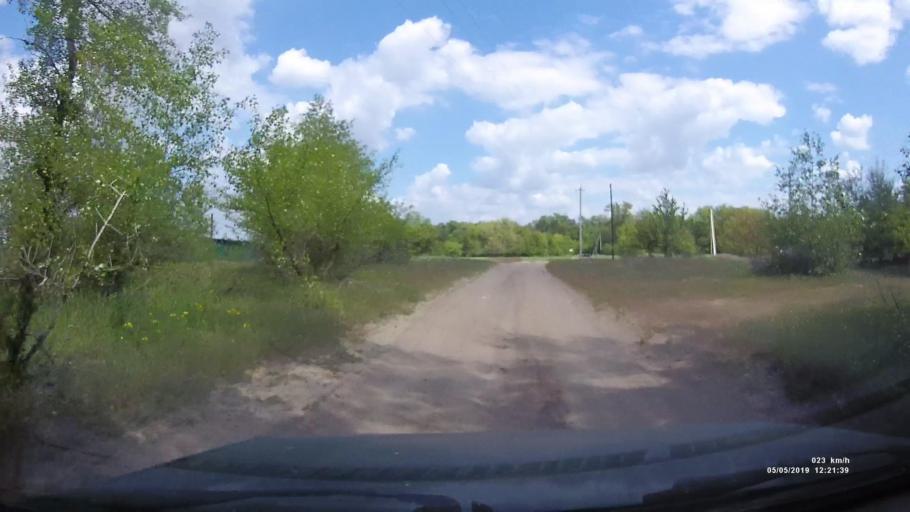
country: RU
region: Rostov
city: Konstantinovsk
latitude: 47.7550
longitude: 41.0384
